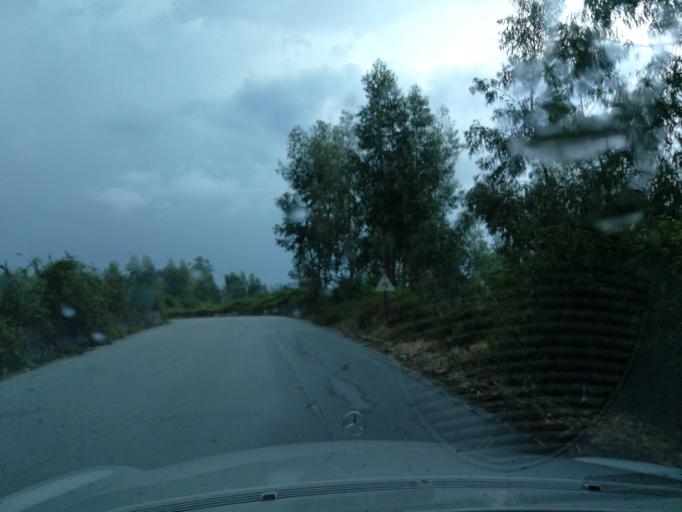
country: PT
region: Braga
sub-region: Vila Nova de Famalicao
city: Joane
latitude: 41.4618
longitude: -8.4353
